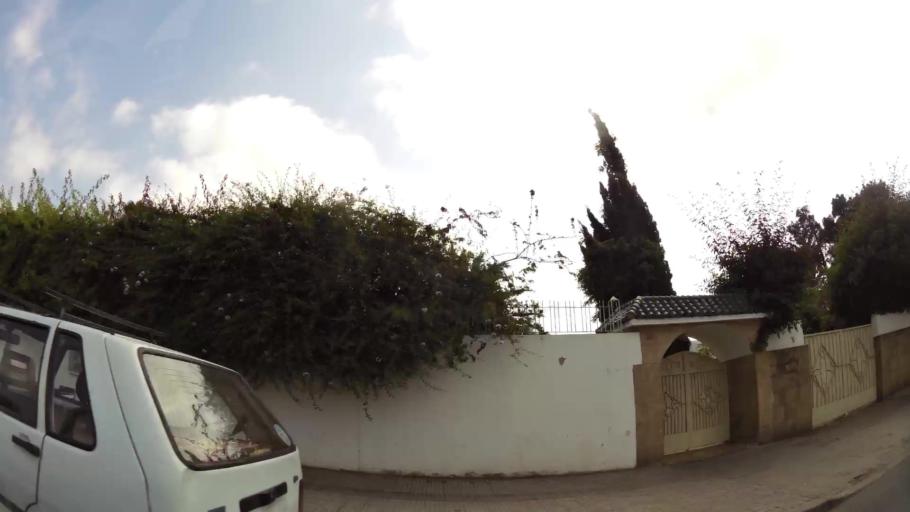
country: MA
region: Rabat-Sale-Zemmour-Zaer
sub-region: Rabat
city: Rabat
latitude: 33.9754
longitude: -6.8468
